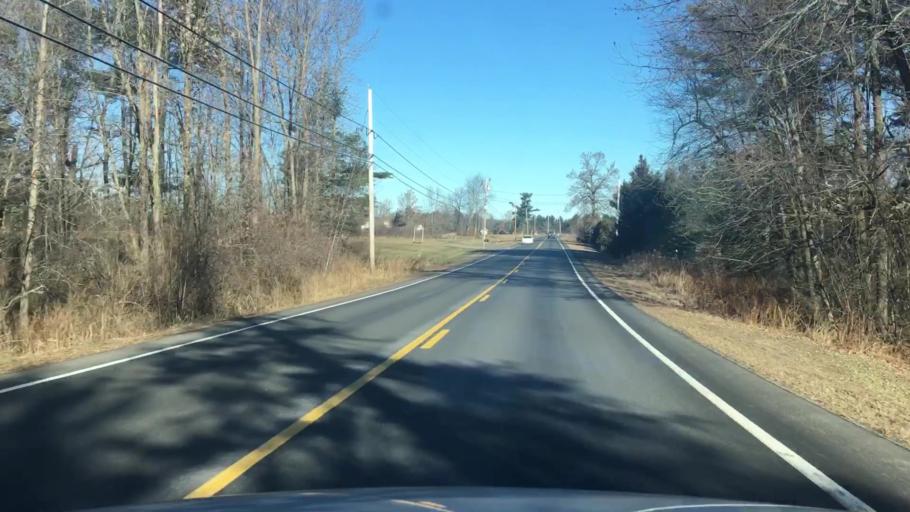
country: US
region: Maine
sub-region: Kennebec County
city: Benton
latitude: 44.5961
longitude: -69.5446
